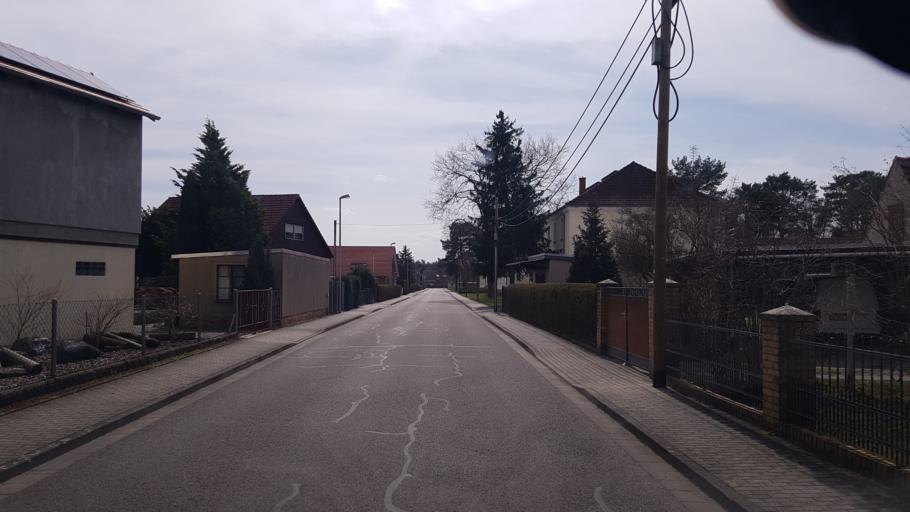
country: DE
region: Brandenburg
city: Schipkau
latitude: 51.5124
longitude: 13.8995
